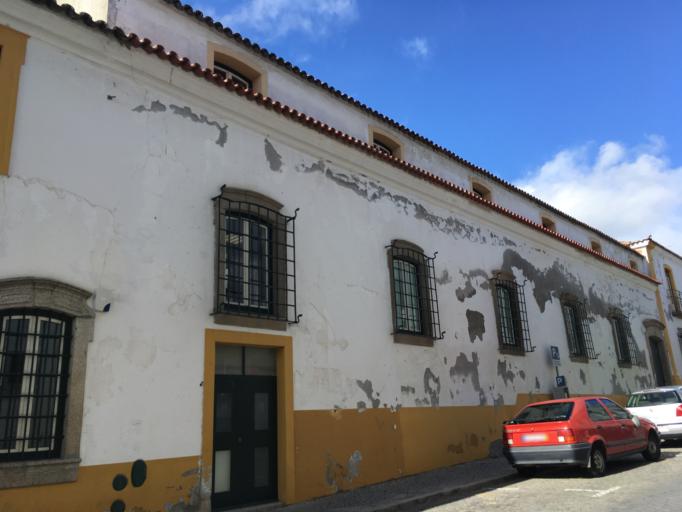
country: PT
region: Evora
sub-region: Evora
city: Evora
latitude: 38.5689
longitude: -7.9120
